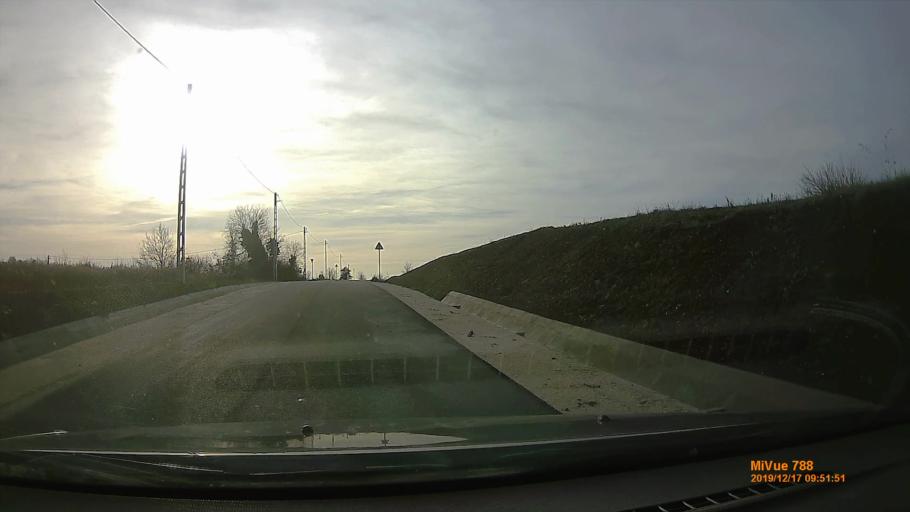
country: HU
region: Somogy
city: Karad
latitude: 46.6196
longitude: 17.7949
